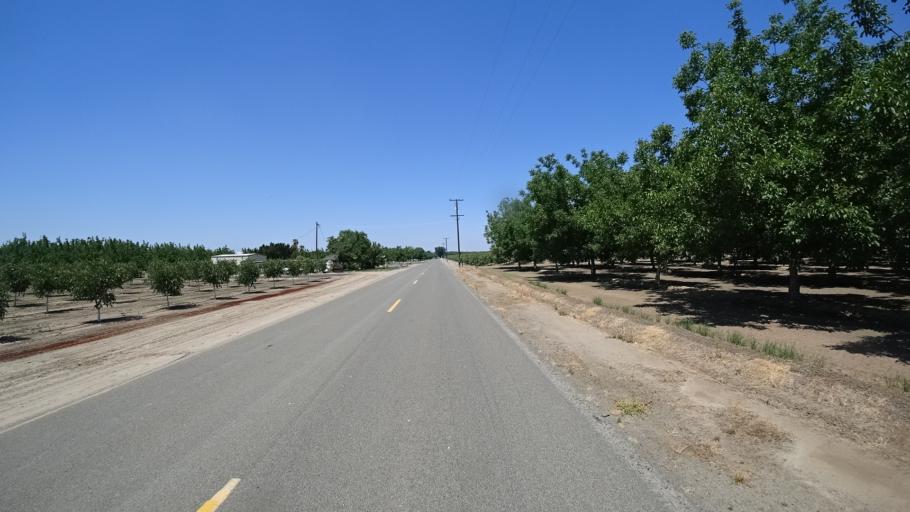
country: US
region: California
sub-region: Kings County
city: Lucerne
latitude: 36.4078
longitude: -119.6549
